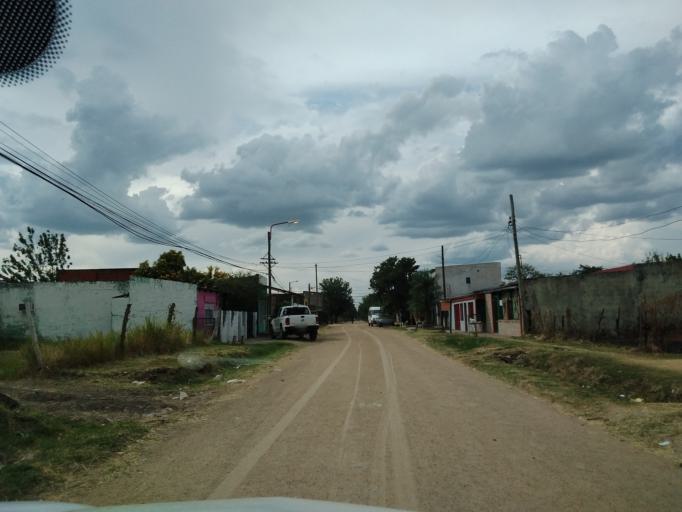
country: AR
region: Corrientes
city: Corrientes
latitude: -27.5229
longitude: -58.7922
